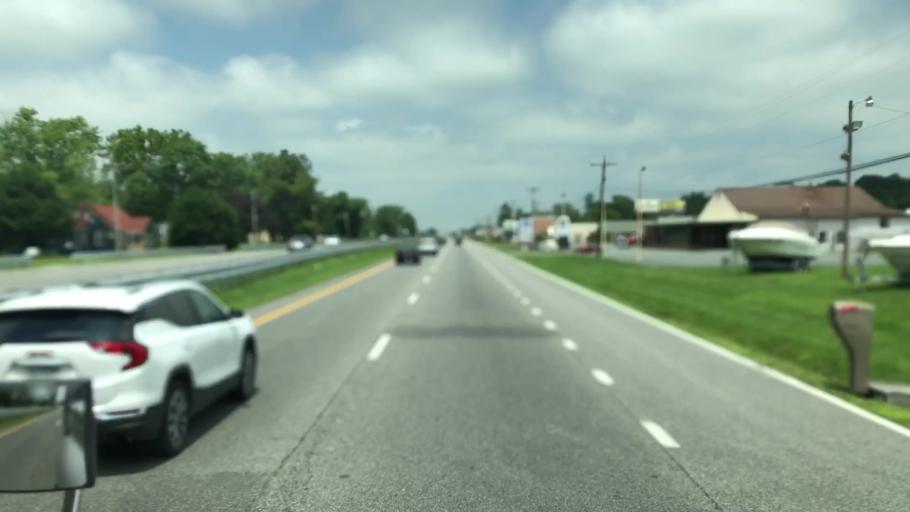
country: US
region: Maryland
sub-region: Talbot County
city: Easton
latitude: 38.8046
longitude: -76.0600
